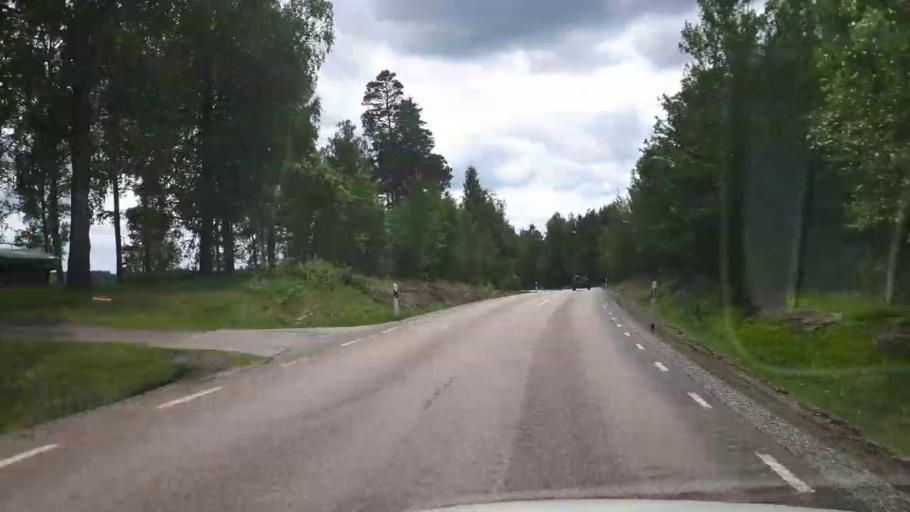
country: SE
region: Vaestmanland
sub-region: Skinnskattebergs Kommun
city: Skinnskatteberg
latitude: 59.8592
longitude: 15.8425
